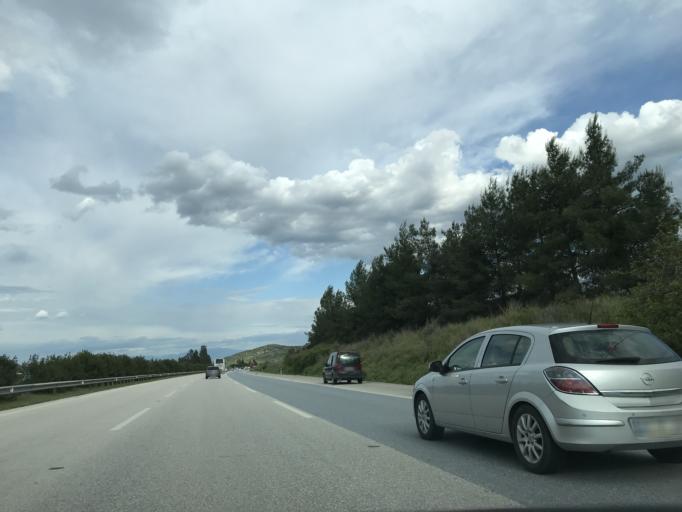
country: TR
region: Adana
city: Yakapinar
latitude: 37.0043
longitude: 35.7144
